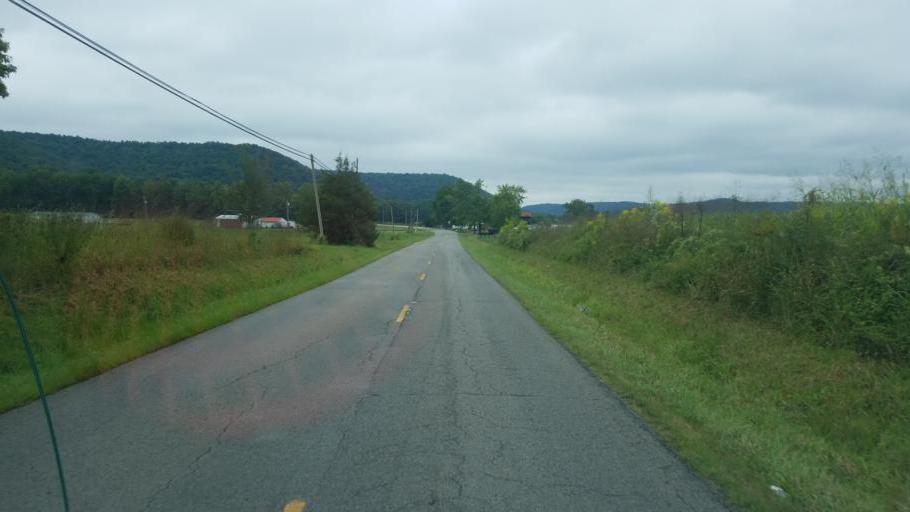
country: US
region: Kentucky
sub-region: Rowan County
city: Morehead
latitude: 38.3240
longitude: -83.5488
